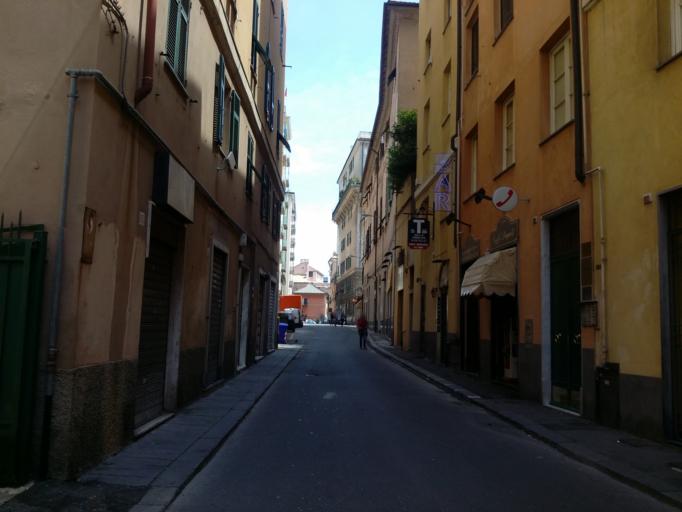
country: IT
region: Liguria
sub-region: Provincia di Genova
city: San Teodoro
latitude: 44.4120
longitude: 8.8911
